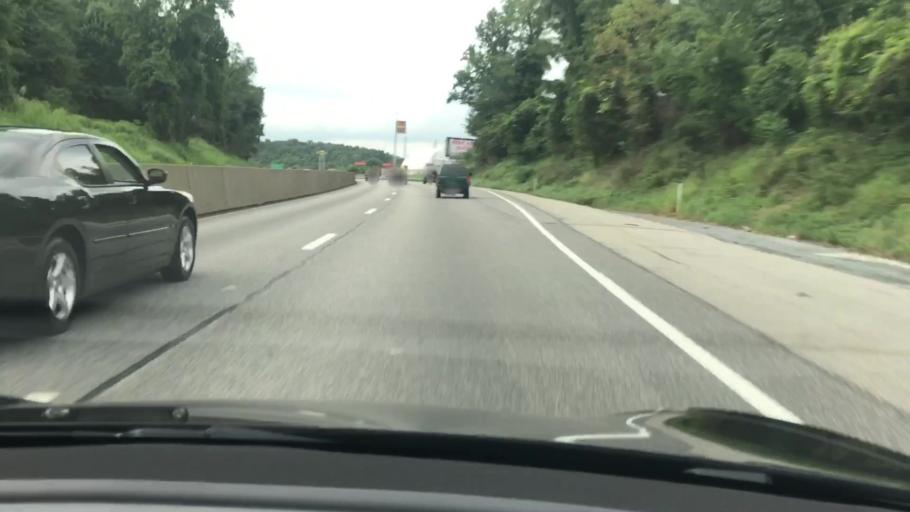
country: US
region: Pennsylvania
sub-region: York County
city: Valley Green
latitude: 40.1274
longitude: -76.7925
